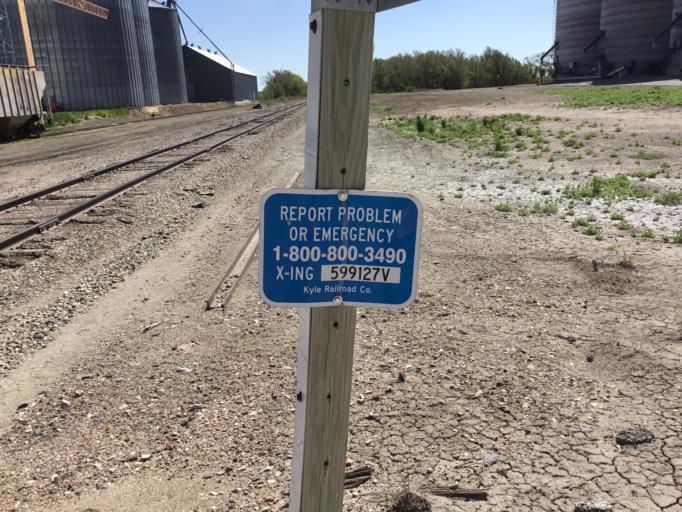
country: US
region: Kansas
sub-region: Smith County
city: Smith Center
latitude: 39.7632
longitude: -98.9216
